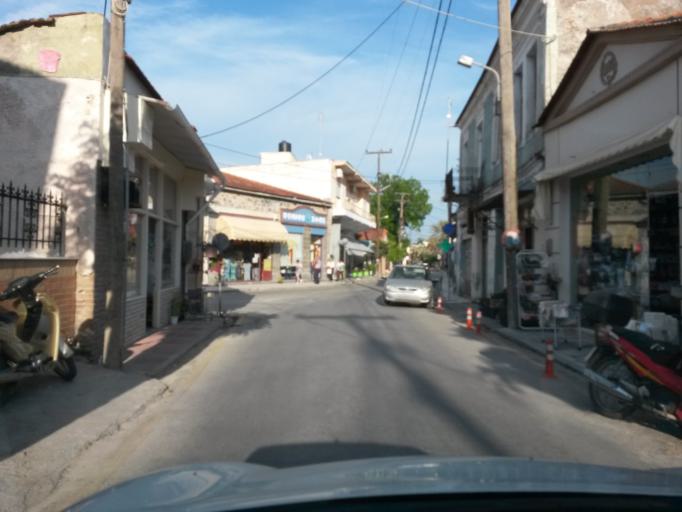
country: GR
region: North Aegean
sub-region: Nomos Lesvou
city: Kalloni
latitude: 39.2331
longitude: 26.2083
